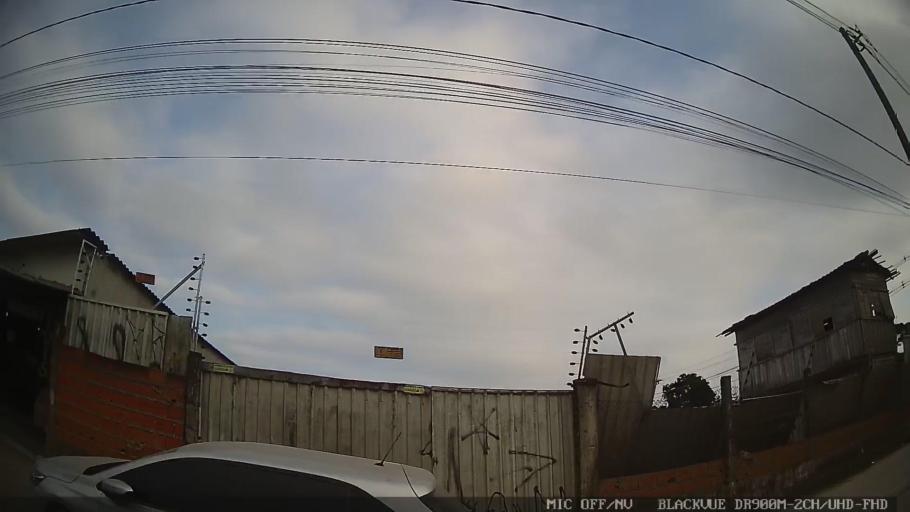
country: BR
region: Sao Paulo
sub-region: Guaruja
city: Guaruja
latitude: -23.9688
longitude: -46.2130
